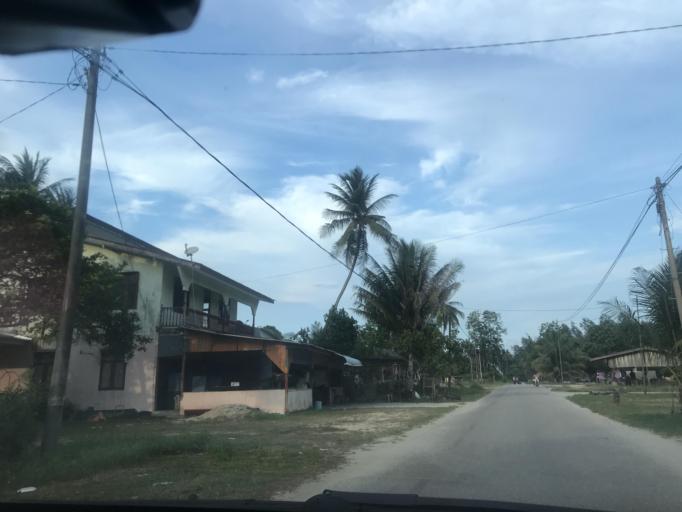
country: MY
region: Kelantan
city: Kota Bharu
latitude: 6.1307
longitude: 102.3648
